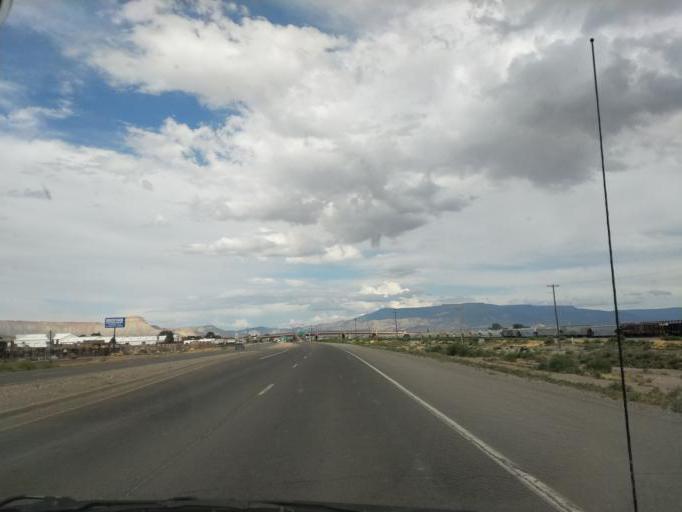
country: US
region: Colorado
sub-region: Mesa County
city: Grand Junction
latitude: 39.0707
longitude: -108.5243
